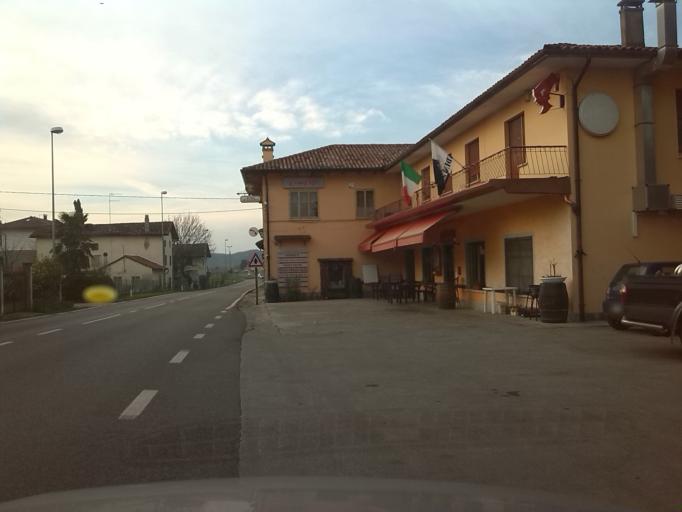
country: IT
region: Friuli Venezia Giulia
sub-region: Provincia di Udine
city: Prepotto
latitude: 46.0423
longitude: 13.4387
